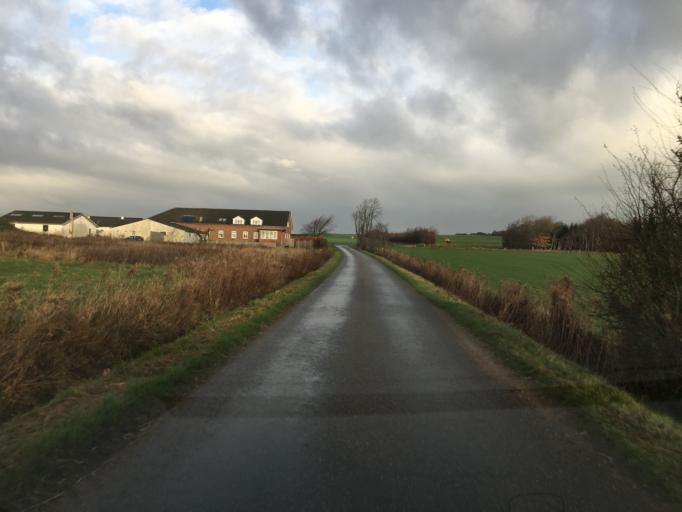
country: DK
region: South Denmark
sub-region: Tonder Kommune
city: Sherrebek
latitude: 55.1533
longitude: 8.8022
